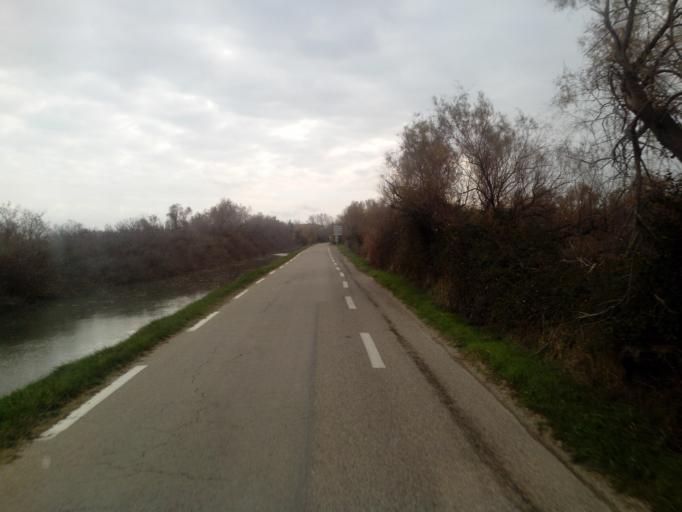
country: FR
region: Languedoc-Roussillon
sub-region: Departement du Gard
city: Vauvert
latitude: 43.6078
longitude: 4.3340
